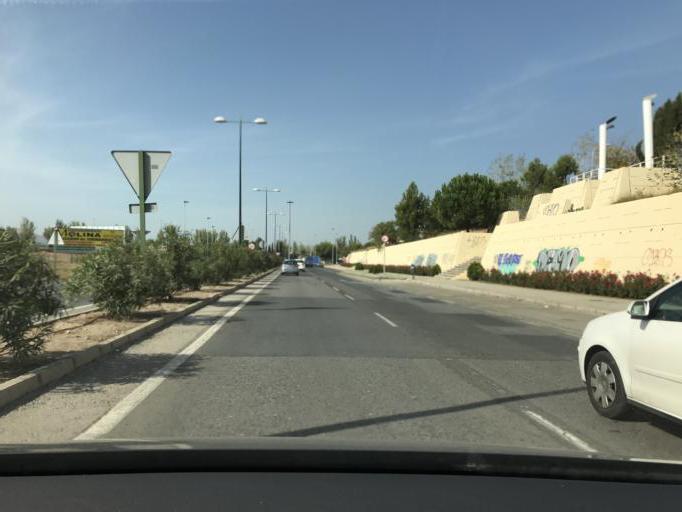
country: ES
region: Andalusia
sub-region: Provincia de Granada
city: Maracena
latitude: 37.2075
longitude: -3.6204
